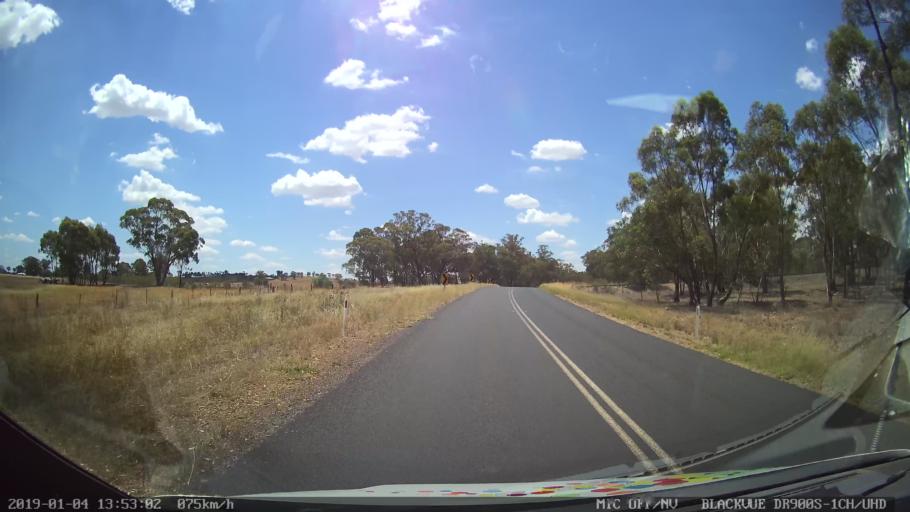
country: AU
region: New South Wales
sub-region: Dubbo Municipality
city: Dubbo
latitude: -32.3873
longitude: 148.5719
